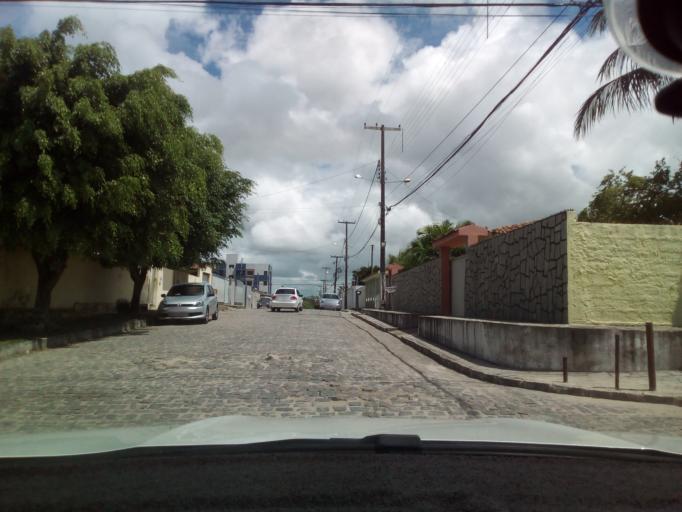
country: BR
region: Paraiba
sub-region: Bayeux
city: Bayeux
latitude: -7.1363
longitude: -34.9376
